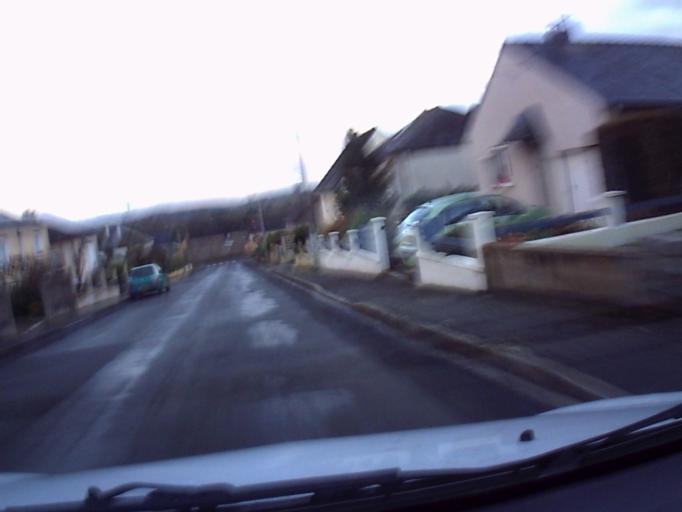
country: FR
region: Brittany
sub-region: Departement d'Ille-et-Vilaine
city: Iffendic
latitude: 48.1305
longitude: -2.0309
